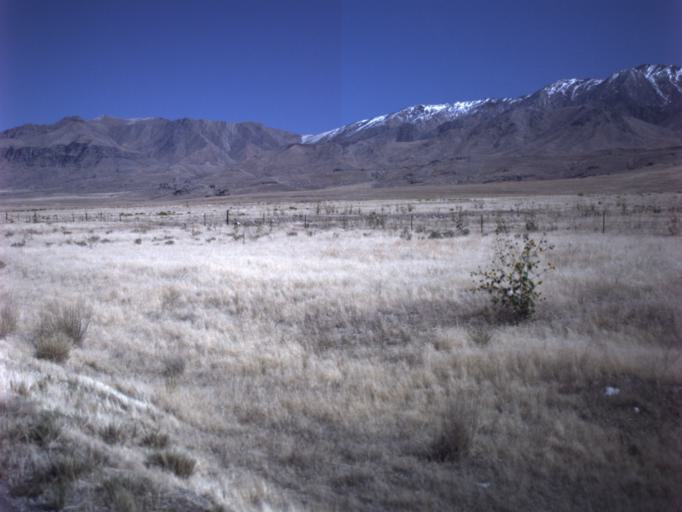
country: US
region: Utah
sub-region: Tooele County
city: Grantsville
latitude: 40.5913
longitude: -112.7202
